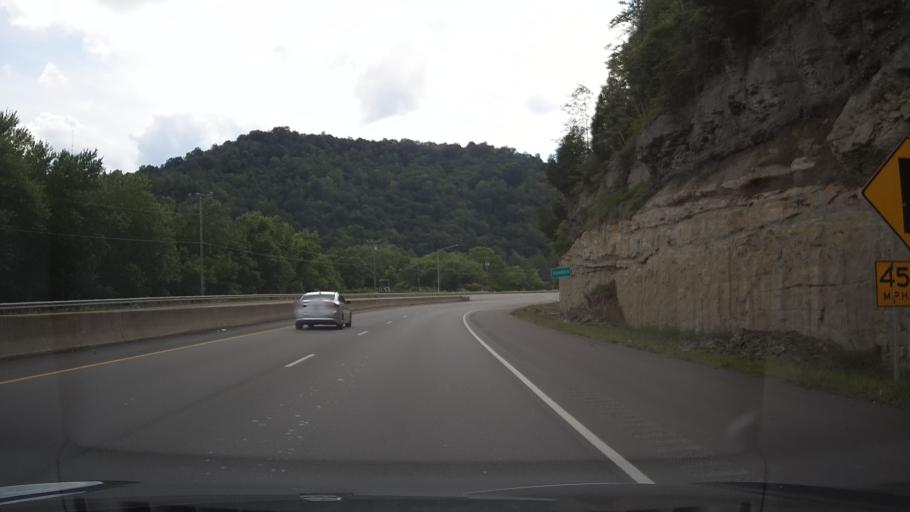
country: US
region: Kentucky
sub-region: Floyd County
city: Prestonsburg
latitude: 37.6035
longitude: -82.6962
